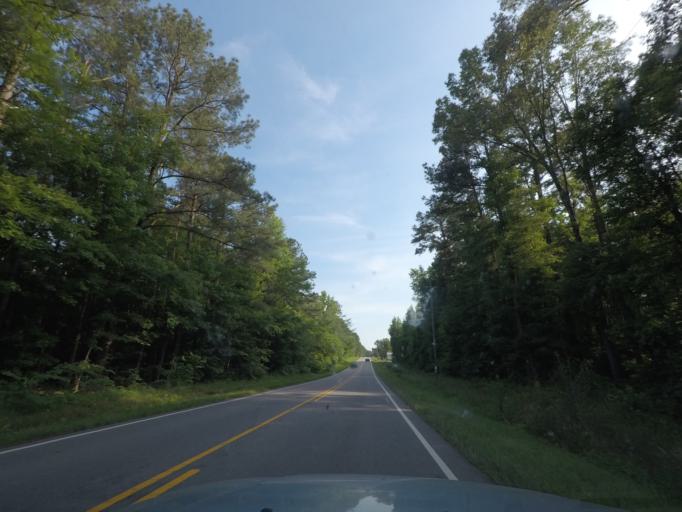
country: US
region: North Carolina
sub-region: Granville County
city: Oxford
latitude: 36.4601
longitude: -78.5632
